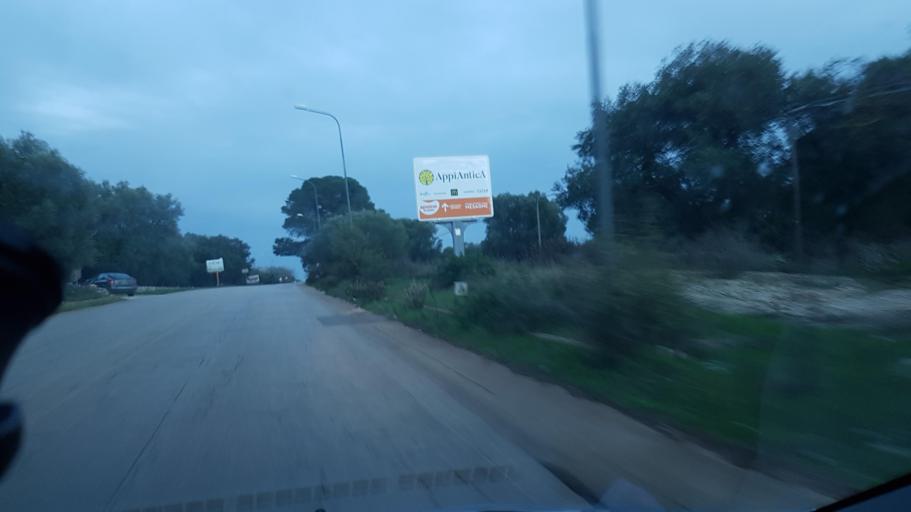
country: IT
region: Apulia
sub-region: Provincia di Brindisi
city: Ceglie Messapica
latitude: 40.6445
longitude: 17.5325
